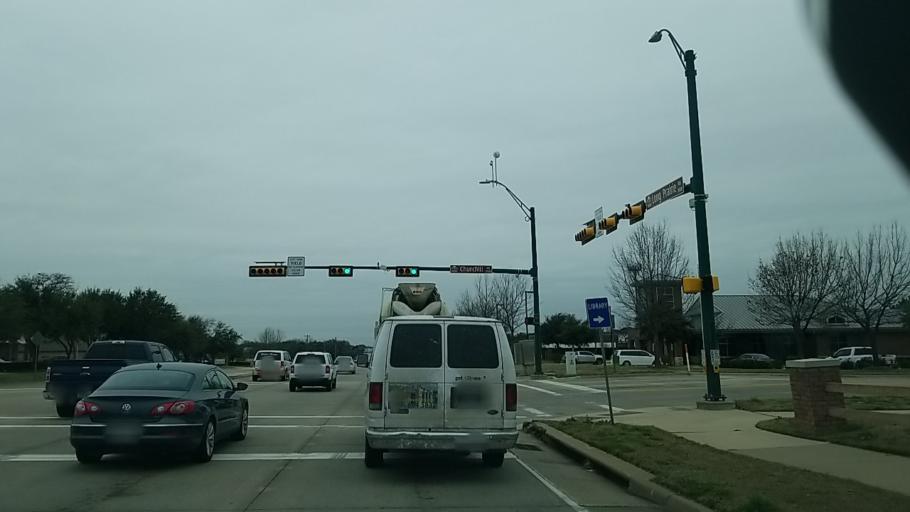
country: US
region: Texas
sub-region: Denton County
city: Flower Mound
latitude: 33.0338
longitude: -97.0708
